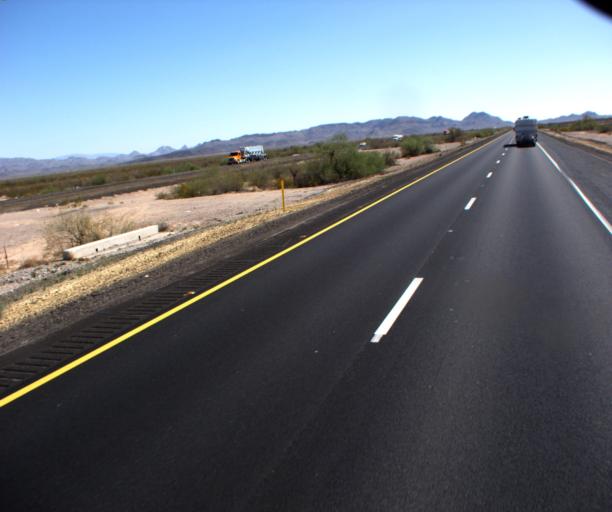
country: US
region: Arizona
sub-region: La Paz County
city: Salome
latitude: 33.6249
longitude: -113.7283
